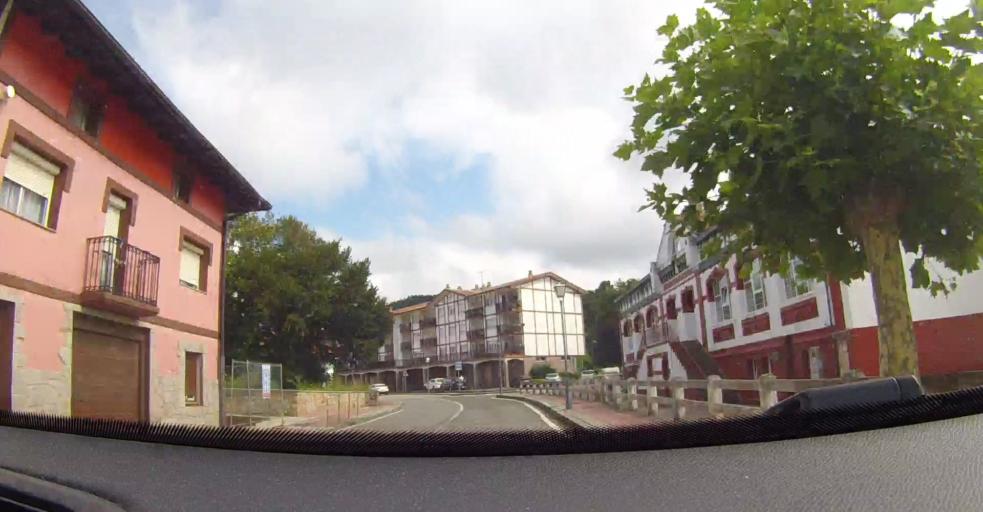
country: ES
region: Basque Country
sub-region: Bizkaia
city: Ibarrangelu
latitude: 43.3907
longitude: -2.6357
